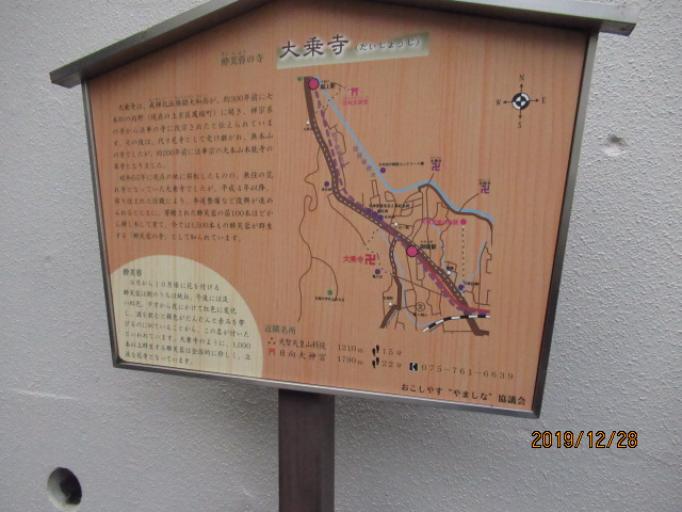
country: JP
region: Kyoto
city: Kyoto
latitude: 34.9955
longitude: 135.7981
